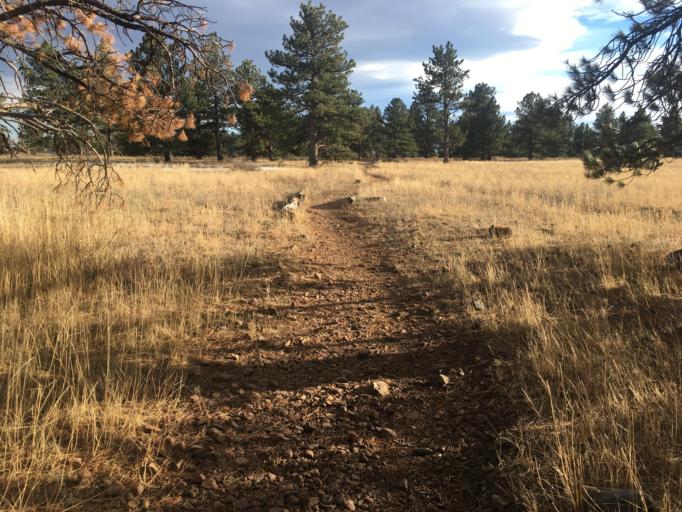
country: US
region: Colorado
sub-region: Boulder County
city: Superior
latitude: 39.9176
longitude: -105.2488
